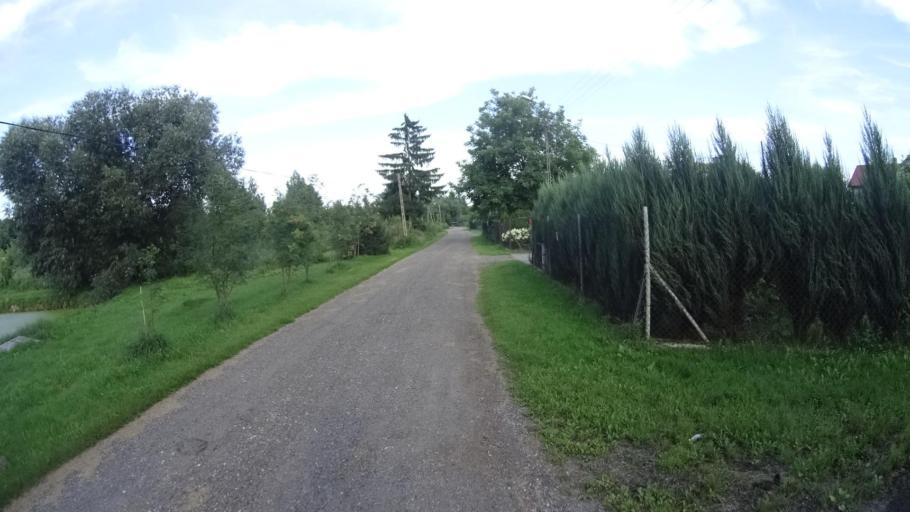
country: PL
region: Masovian Voivodeship
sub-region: Powiat piaseczynski
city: Tarczyn
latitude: 51.9770
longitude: 20.8410
